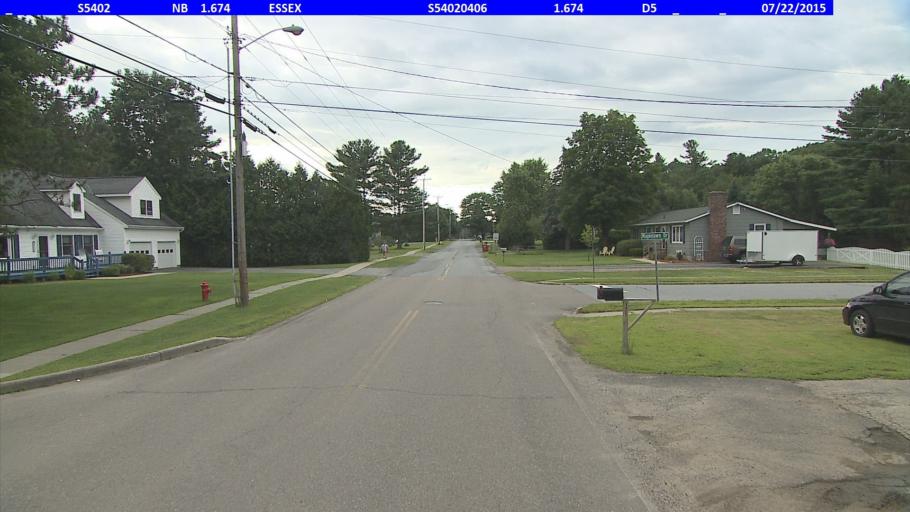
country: US
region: Vermont
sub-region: Chittenden County
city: Jericho
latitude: 44.5021
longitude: -73.0501
